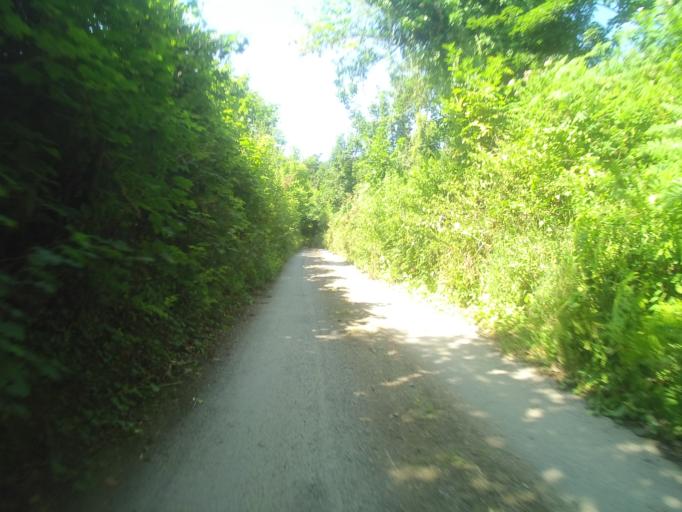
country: GB
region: England
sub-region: Devon
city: Dartmouth
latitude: 50.3568
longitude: -3.6043
